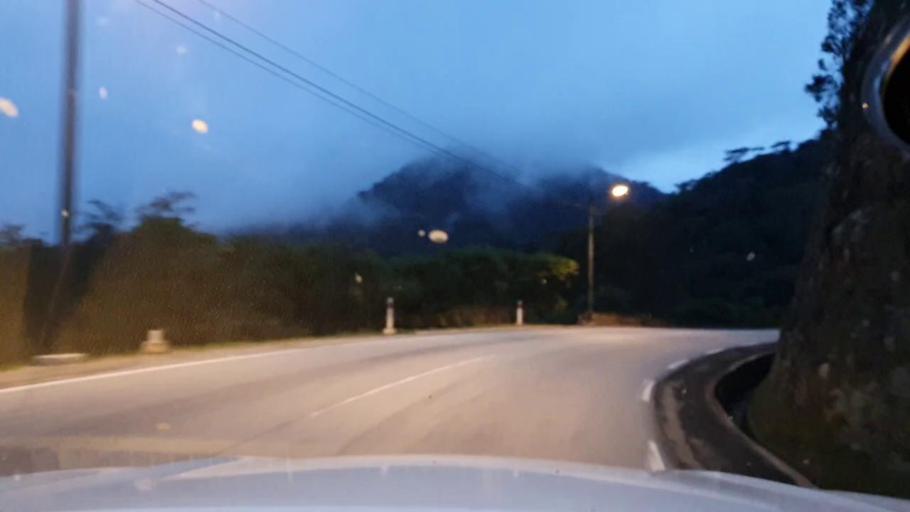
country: RW
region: Southern Province
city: Nzega
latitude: -2.5258
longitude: 29.3799
